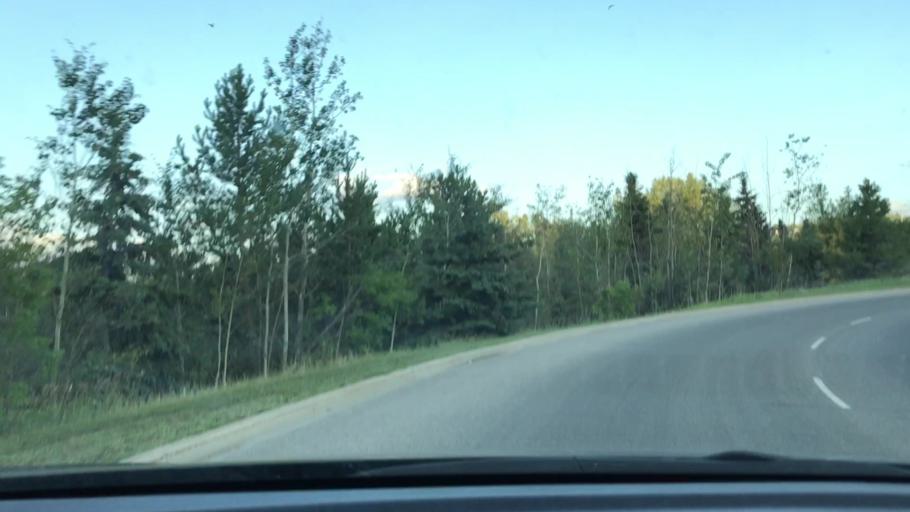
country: CA
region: Alberta
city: Edmonton
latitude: 53.5377
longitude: -113.4825
